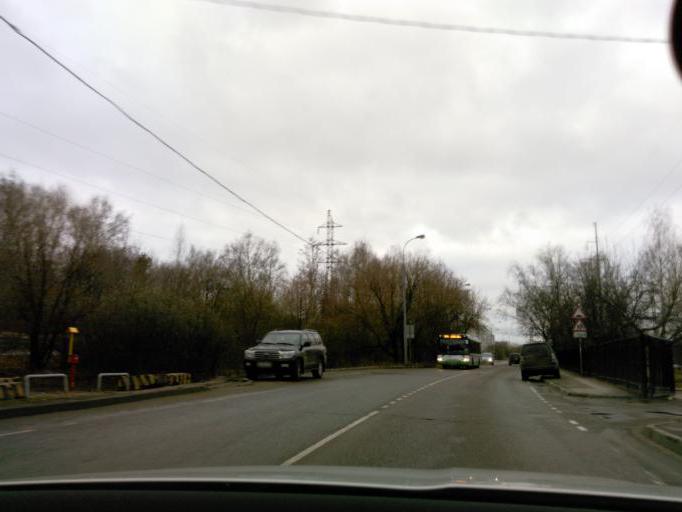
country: RU
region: Moskovskaya
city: Levoberezhnaya
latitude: 55.8779
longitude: 37.4734
